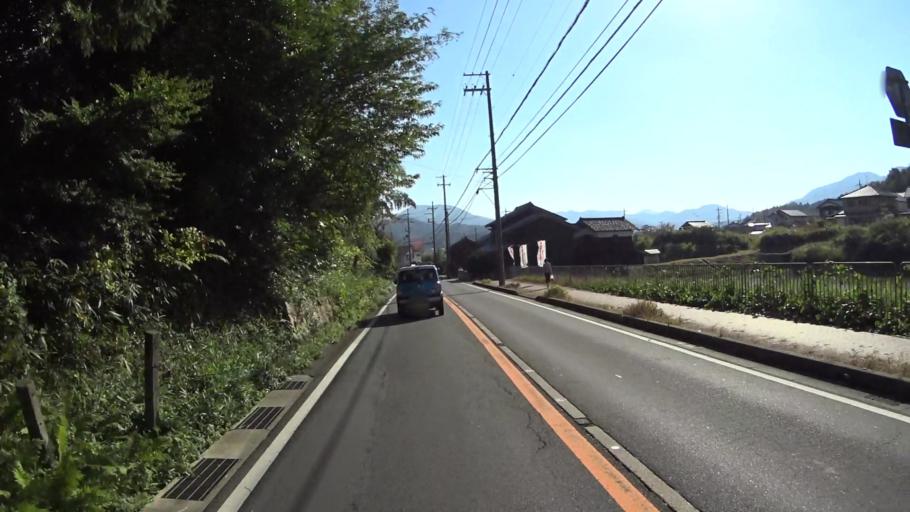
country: JP
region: Kyoto
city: Miyazu
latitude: 35.6164
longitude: 135.0608
